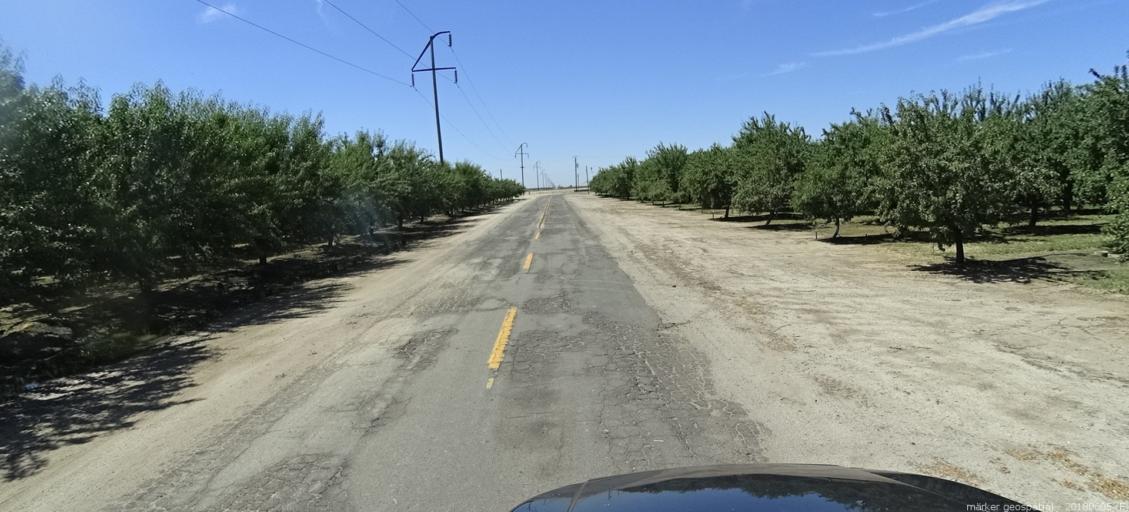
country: US
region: California
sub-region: Madera County
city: Chowchilla
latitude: 37.0996
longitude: -120.3471
